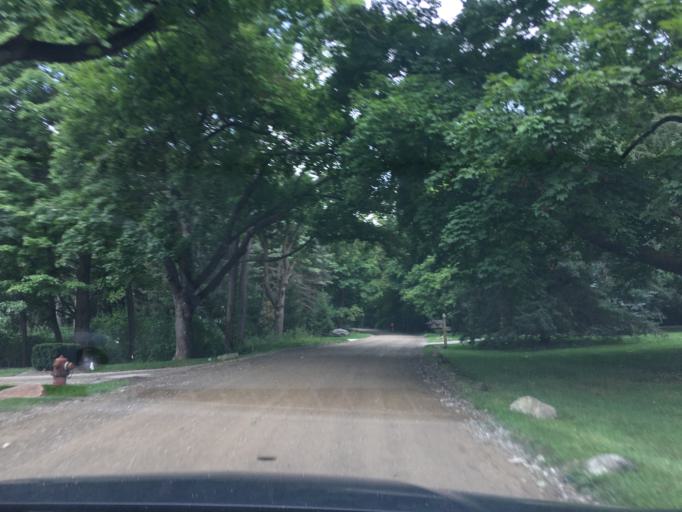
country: US
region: Michigan
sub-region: Oakland County
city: Bloomfield Hills
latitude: 42.5784
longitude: -83.2339
